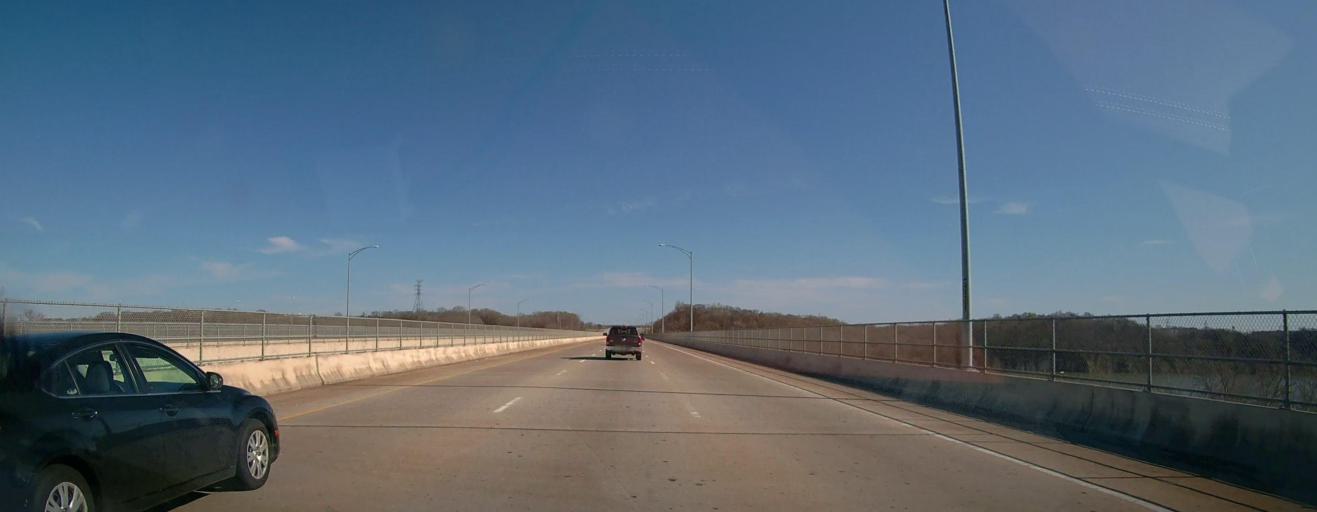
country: US
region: Alabama
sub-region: Lauderdale County
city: East Florence
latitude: 34.7960
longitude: -87.6465
